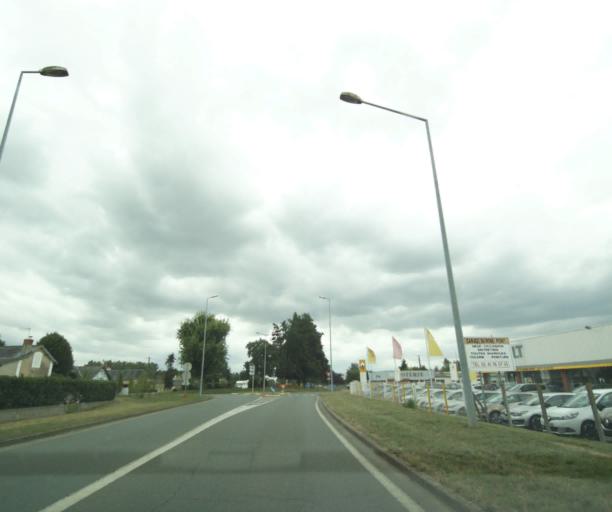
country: FR
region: Pays de la Loire
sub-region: Departement de Maine-et-Loire
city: Durtal
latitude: 47.6604
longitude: -0.2465
